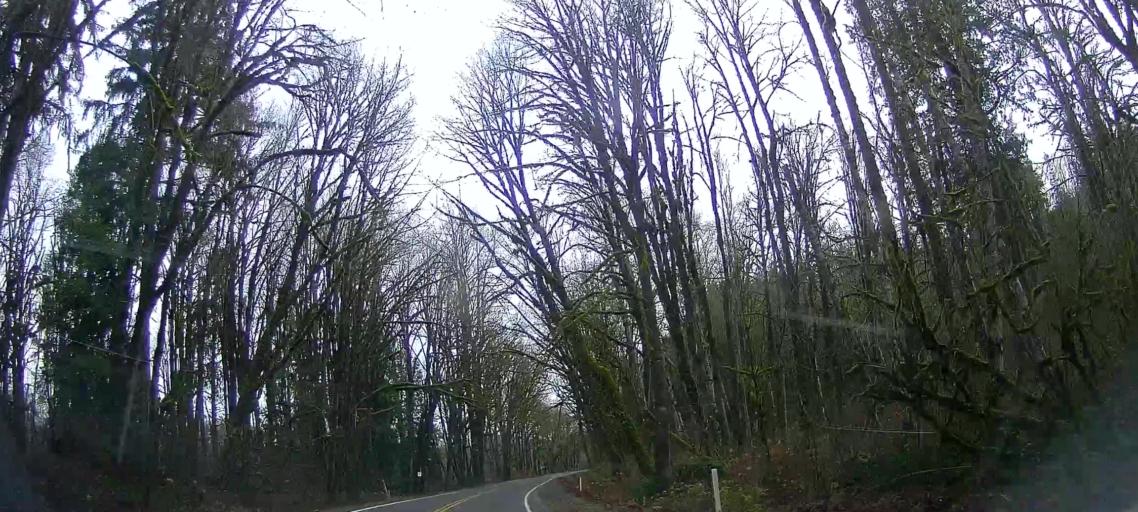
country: US
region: Washington
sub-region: Snohomish County
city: Darrington
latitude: 48.5175
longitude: -121.8639
